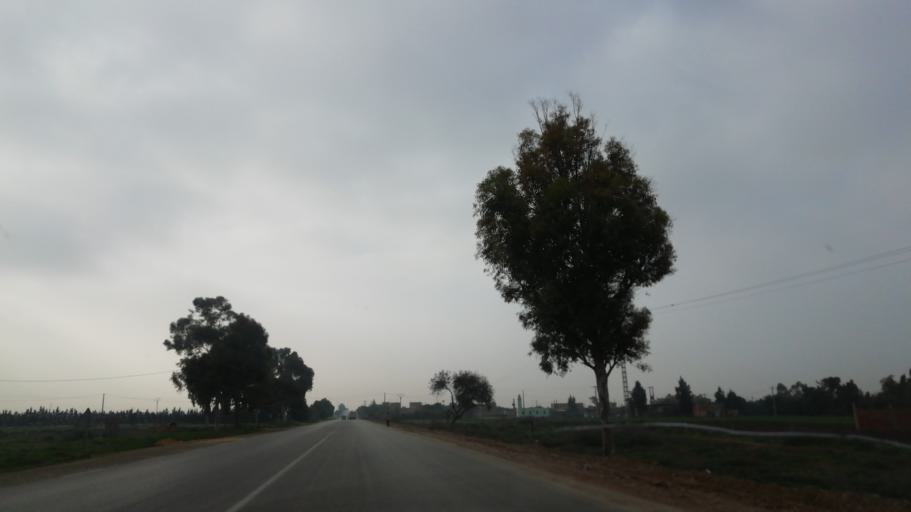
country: DZ
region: Relizane
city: Djidiouia
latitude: 35.8877
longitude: 0.7335
